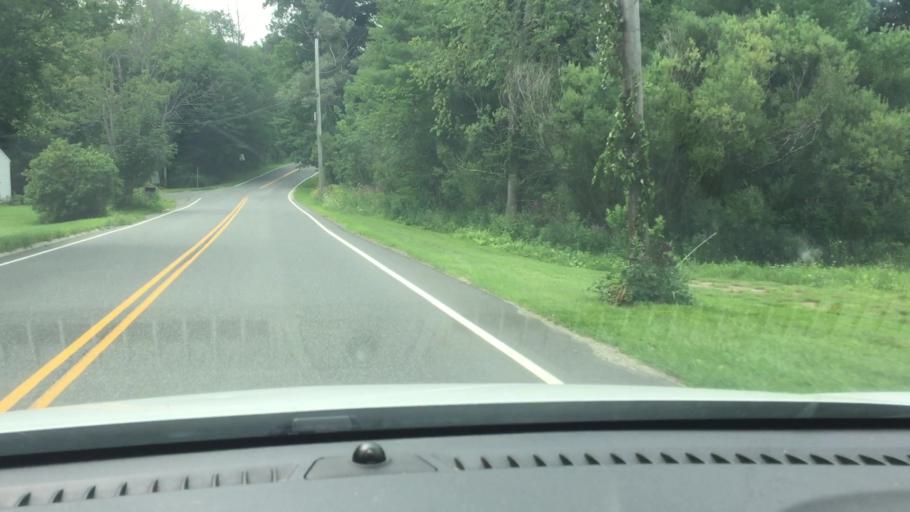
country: US
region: Massachusetts
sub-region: Berkshire County
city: Pittsfield
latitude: 42.4064
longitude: -73.2535
